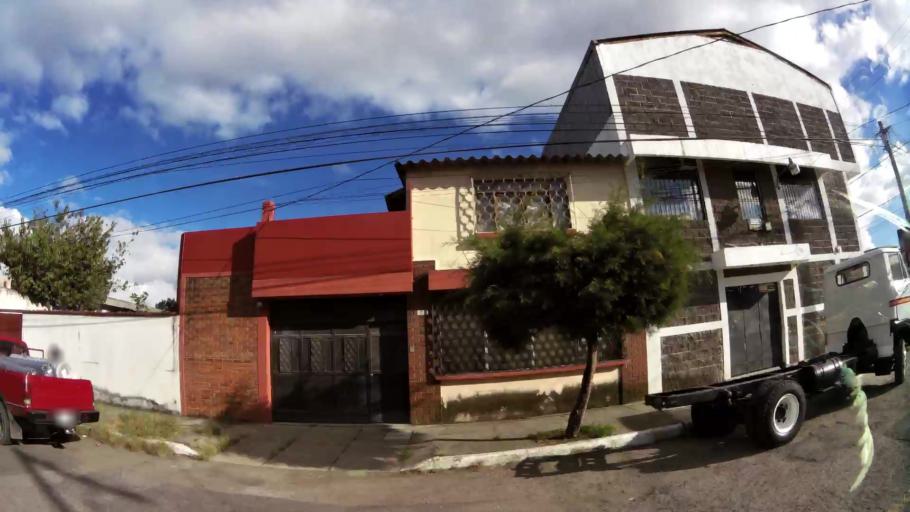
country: GT
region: Guatemala
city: Guatemala City
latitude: 14.6142
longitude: -90.5510
